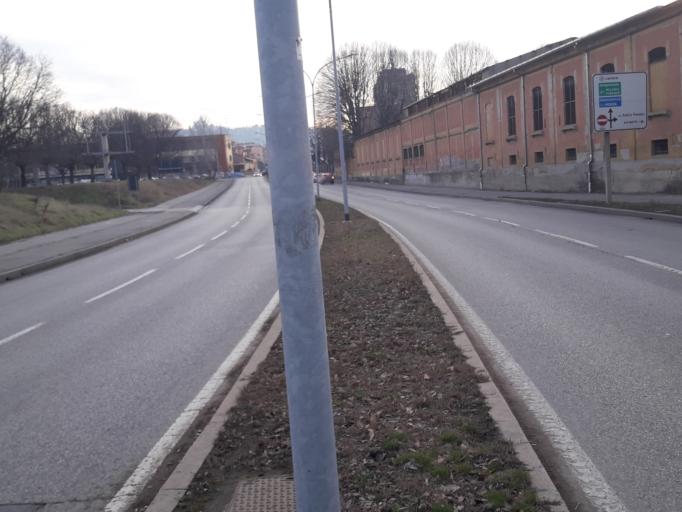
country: IT
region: Emilia-Romagna
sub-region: Provincia di Bologna
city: Bologna
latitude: 44.5074
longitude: 11.3103
